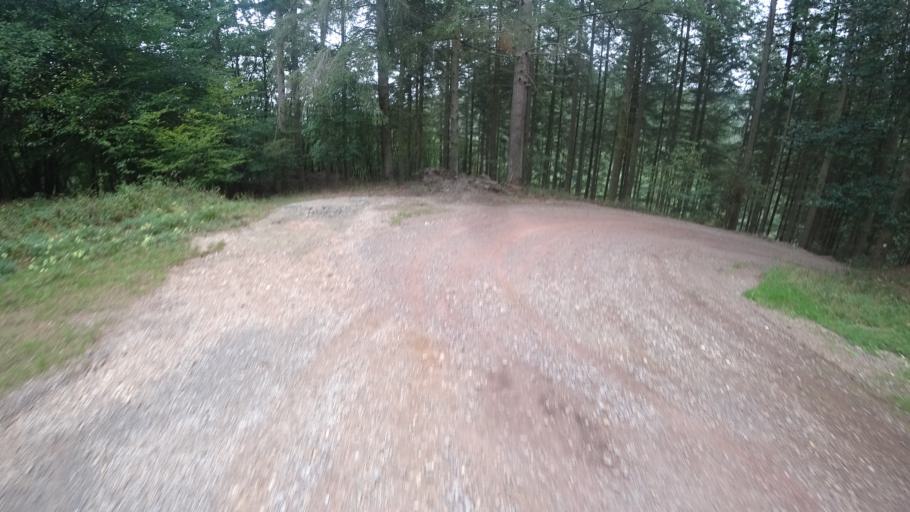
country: DE
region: Rheinland-Pfalz
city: Beulich
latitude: 50.1831
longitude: 7.4600
